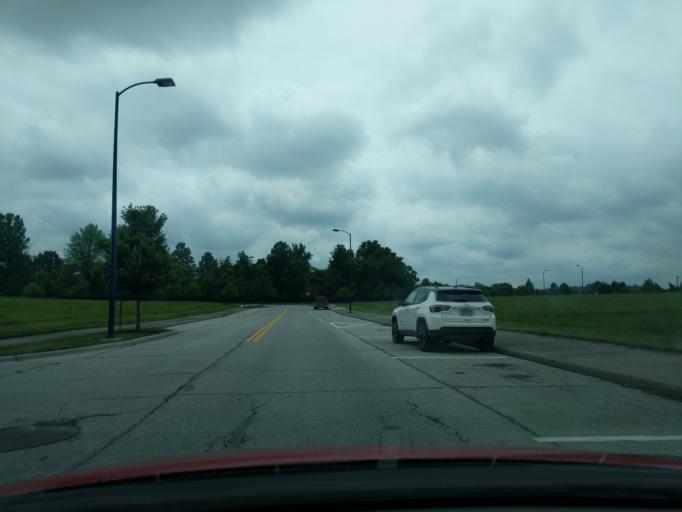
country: US
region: Ohio
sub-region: Franklin County
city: Minerva Park
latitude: 40.0464
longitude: -82.9177
